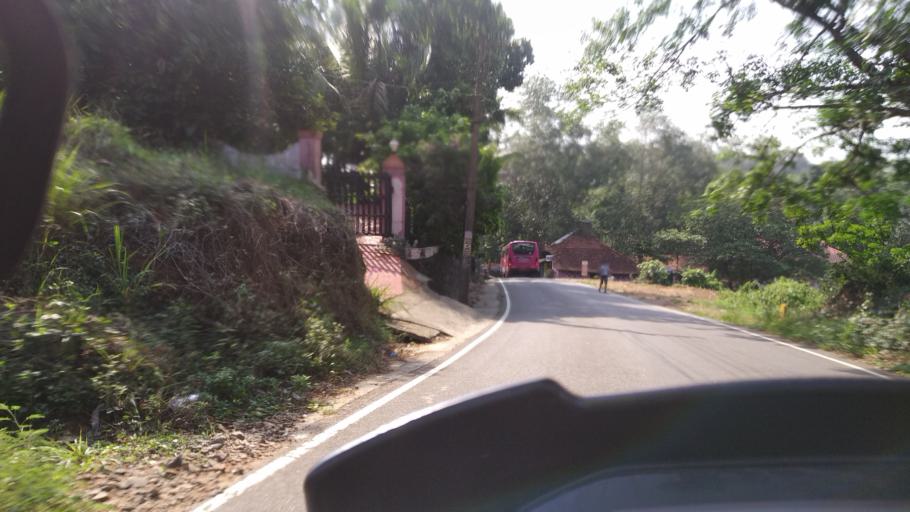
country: IN
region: Kerala
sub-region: Ernakulam
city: Piravam
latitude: 9.8113
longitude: 76.5631
